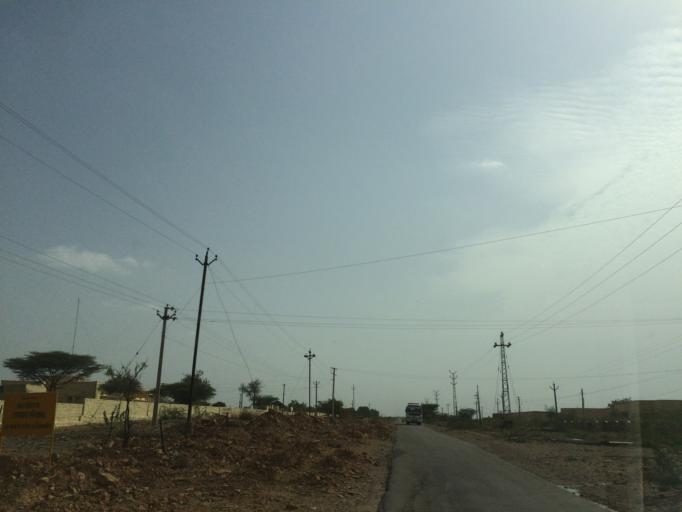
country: IN
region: Rajasthan
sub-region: Jaisalmer
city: Jaisalmer
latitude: 26.9050
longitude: 70.9344
